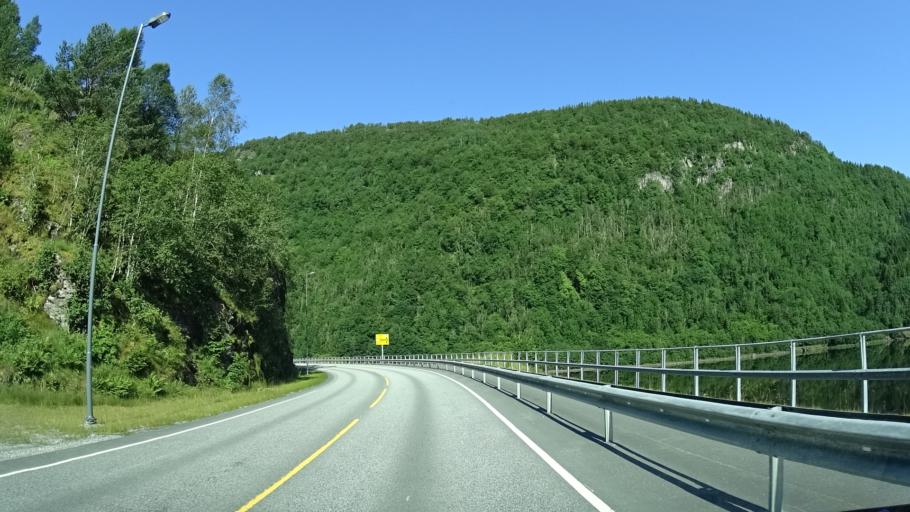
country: NO
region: Hordaland
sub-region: Samnanger
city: Tysse
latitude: 60.3795
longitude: 5.7915
